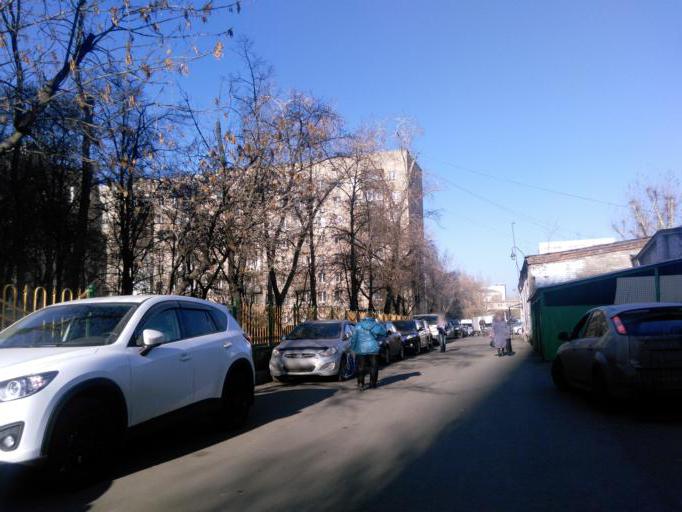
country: RU
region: Moscow
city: Mar'ina Roshcha
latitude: 55.7955
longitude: 37.5862
